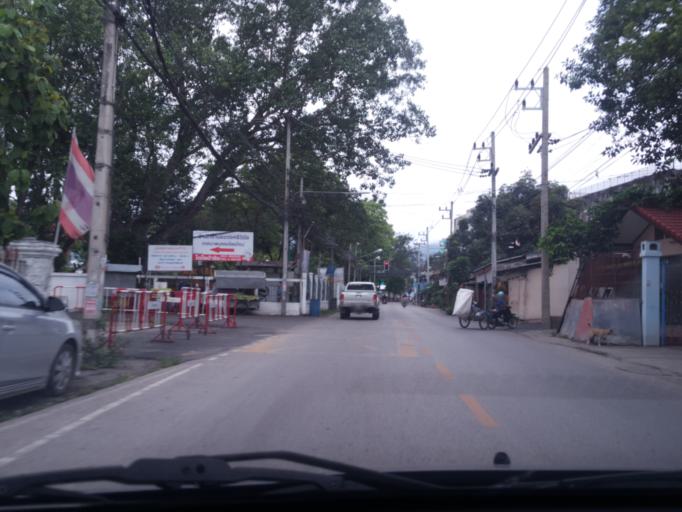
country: TH
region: Chiang Mai
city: Chiang Mai
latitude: 18.8013
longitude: 98.9820
